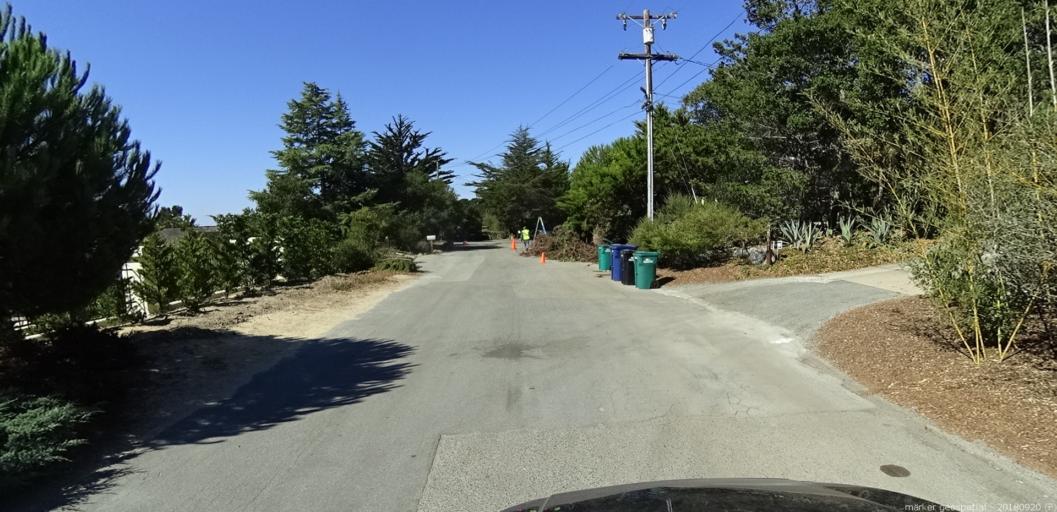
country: US
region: California
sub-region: Monterey County
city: Carmel-by-the-Sea
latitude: 36.5505
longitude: -121.9007
